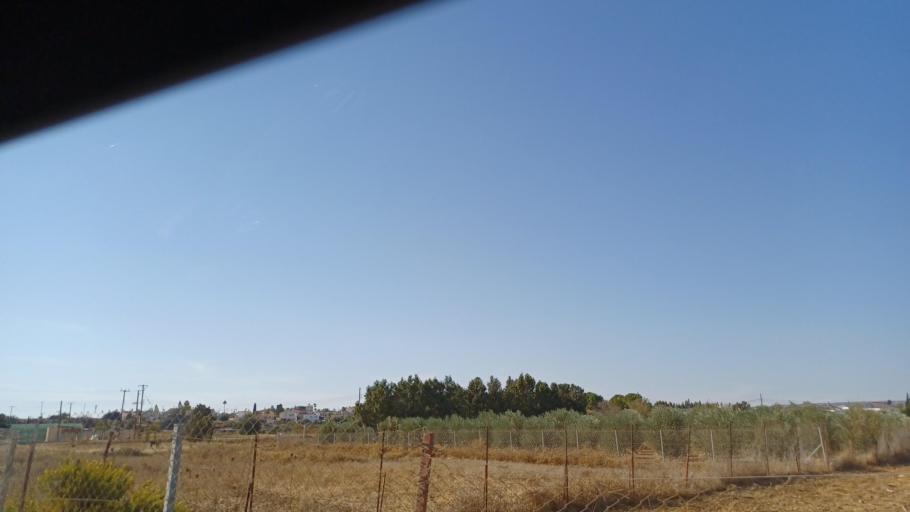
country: CY
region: Larnaka
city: Kolossi
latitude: 34.6722
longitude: 32.9493
